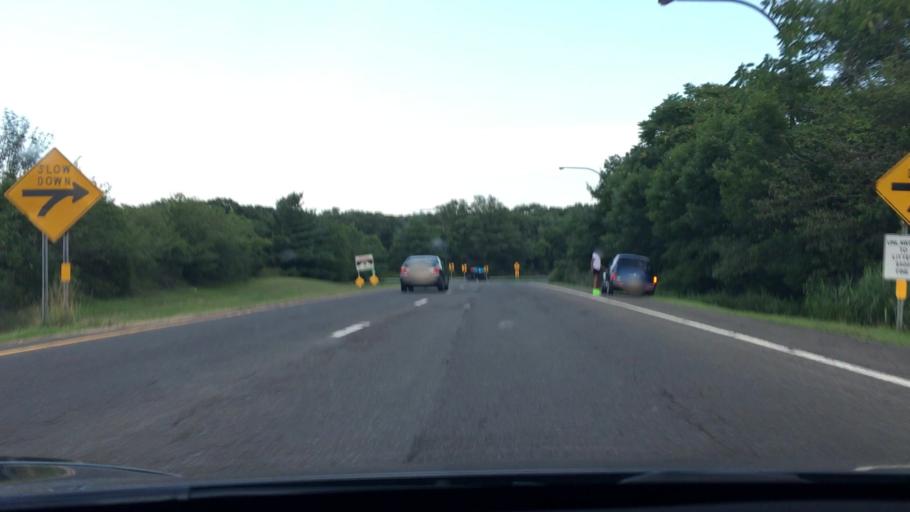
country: US
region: New York
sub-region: Suffolk County
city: Brentwood
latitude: 40.8025
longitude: -73.2815
